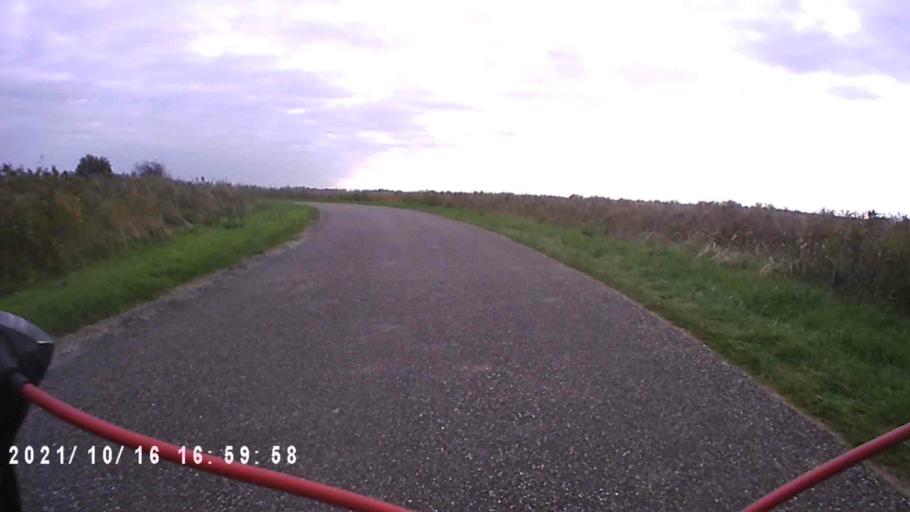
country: NL
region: Friesland
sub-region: Gemeente Dongeradeel
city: Anjum
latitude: 53.3542
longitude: 6.1510
